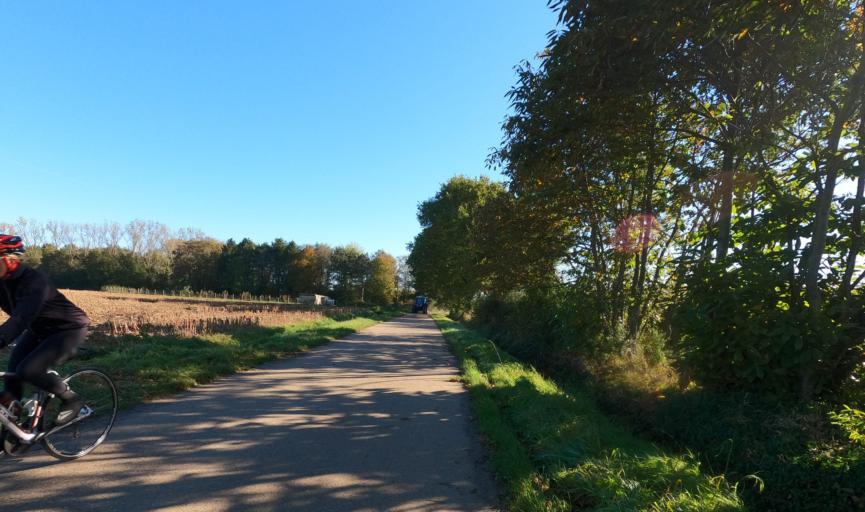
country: BE
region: Flanders
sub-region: Provincie Antwerpen
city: Heist-op-den-Berg
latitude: 51.1036
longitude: 4.7478
